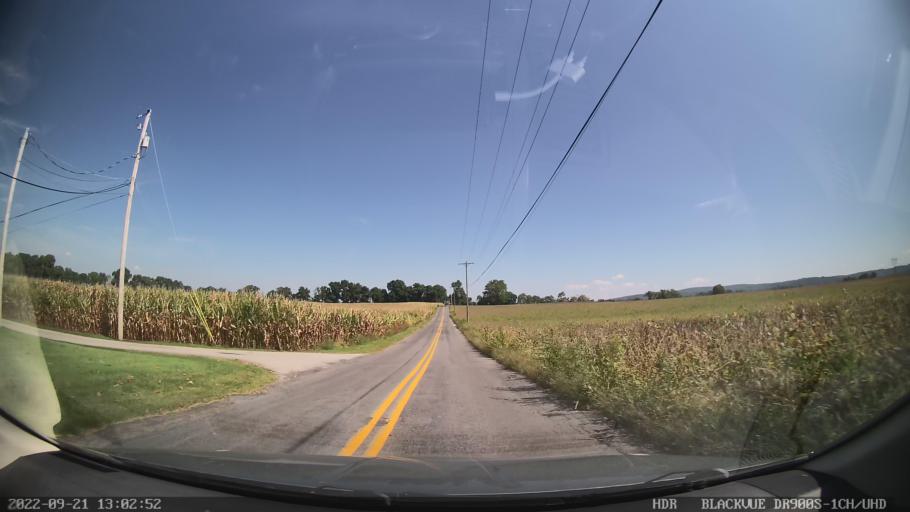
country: US
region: Pennsylvania
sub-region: Berks County
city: Kutztown
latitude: 40.4960
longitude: -75.7608
